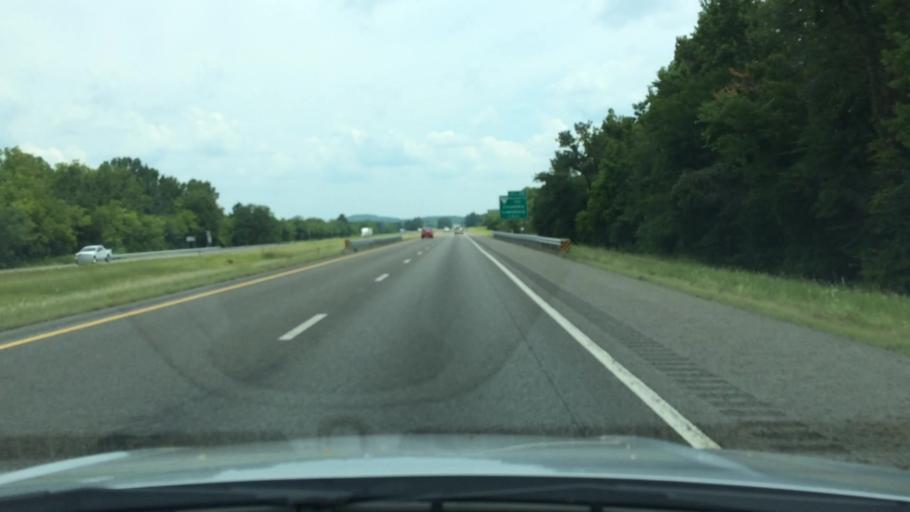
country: US
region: Tennessee
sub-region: Marshall County
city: Cornersville
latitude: 35.4321
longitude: -86.8800
